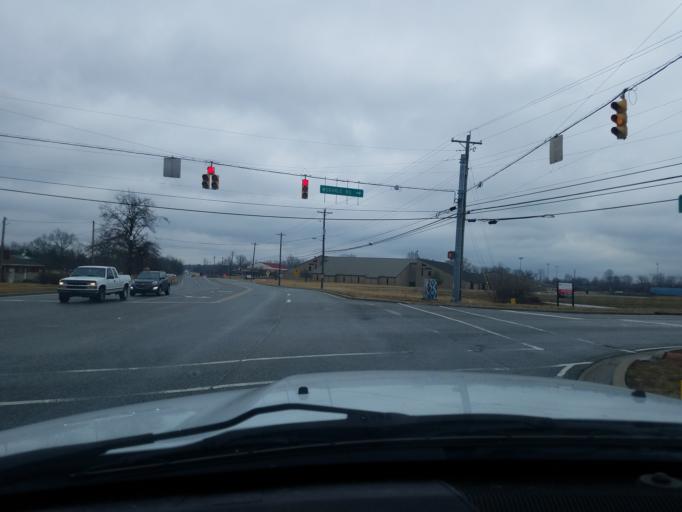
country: US
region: Indiana
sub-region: Clark County
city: Clarksville
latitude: 38.3282
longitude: -85.7366
